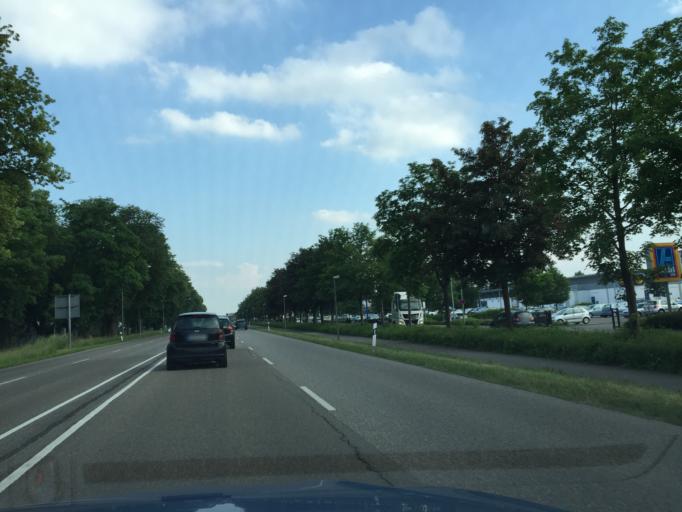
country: DE
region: Bavaria
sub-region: Swabia
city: Neu-Ulm
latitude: 48.3781
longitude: 10.0067
